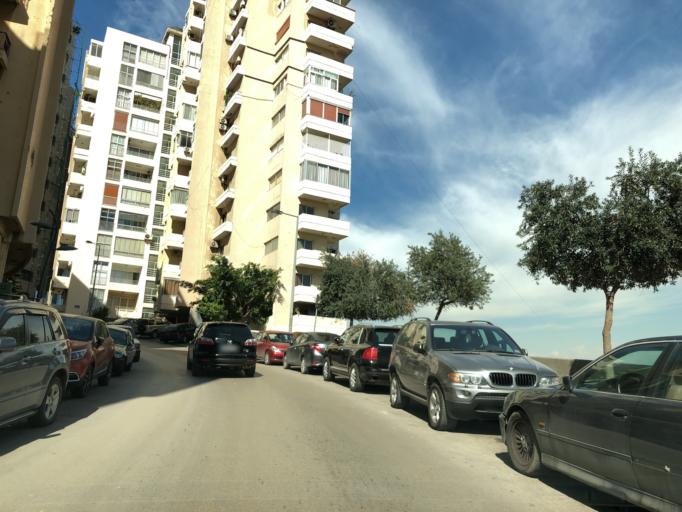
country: LB
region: Mont-Liban
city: Jdaidet el Matn
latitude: 33.8864
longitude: 35.5312
